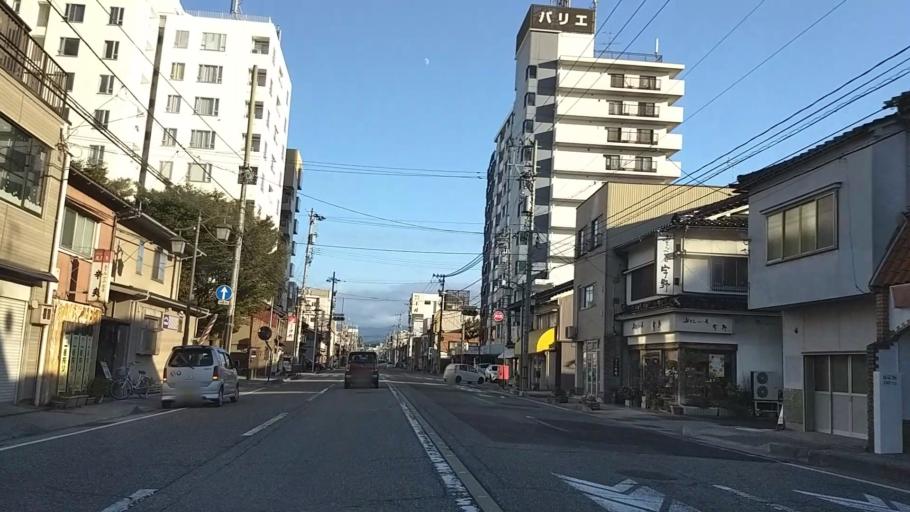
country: JP
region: Ishikawa
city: Nonoichi
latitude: 36.5516
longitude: 136.6544
